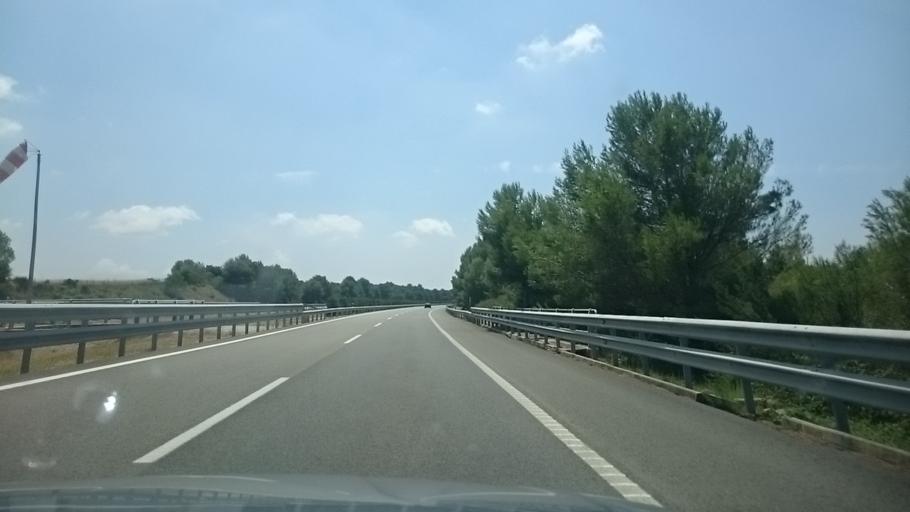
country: ES
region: Catalonia
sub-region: Provincia de Tarragona
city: El Pla de Santa Maria
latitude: 41.3425
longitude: 1.3212
